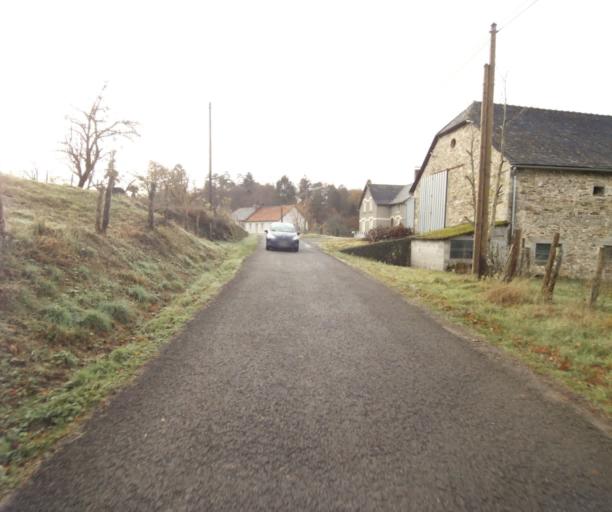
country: FR
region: Limousin
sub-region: Departement de la Correze
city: Cornil
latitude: 45.2041
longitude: 1.7072
